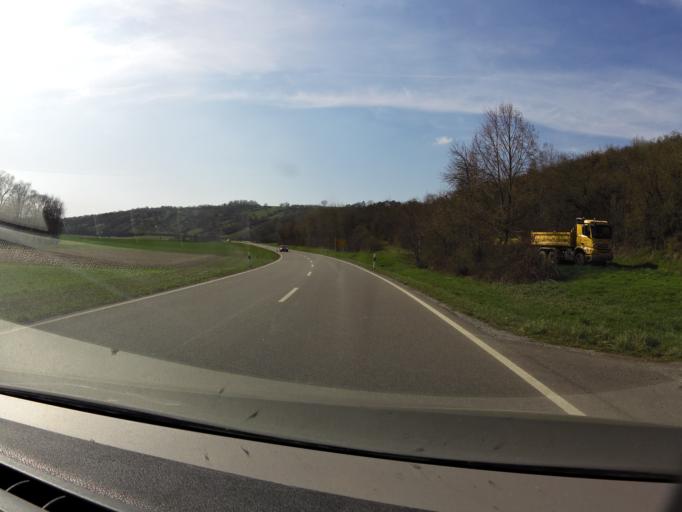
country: DE
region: Bavaria
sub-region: Regierungsbezirk Unterfranken
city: Bieberehren
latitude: 49.5220
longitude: 9.9996
